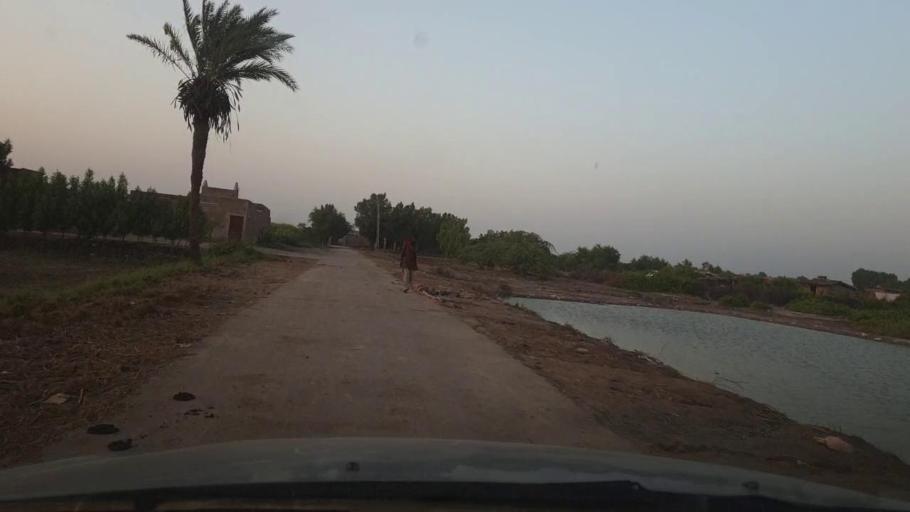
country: PK
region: Sindh
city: Tando Ghulam Ali
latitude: 25.1153
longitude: 68.9886
